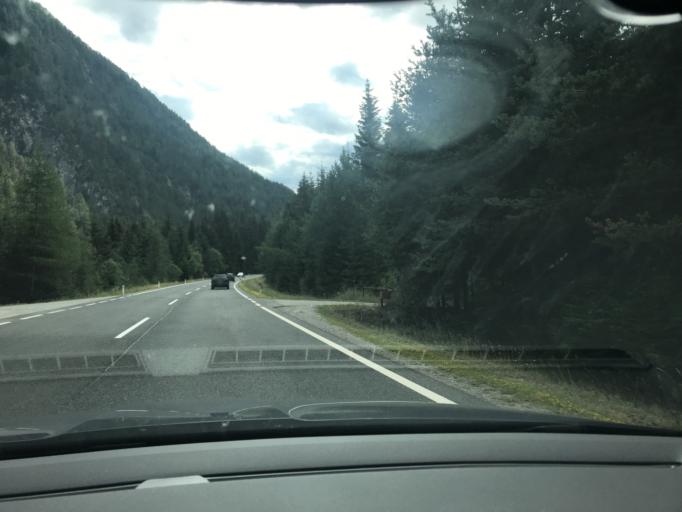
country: AT
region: Tyrol
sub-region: Politischer Bezirk Lienz
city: Anras
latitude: 46.7626
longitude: 12.5637
